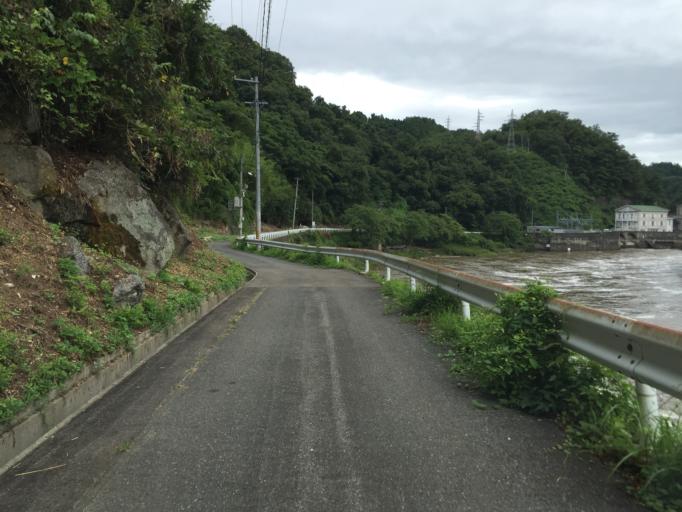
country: JP
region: Fukushima
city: Fukushima-shi
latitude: 37.7198
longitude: 140.4943
